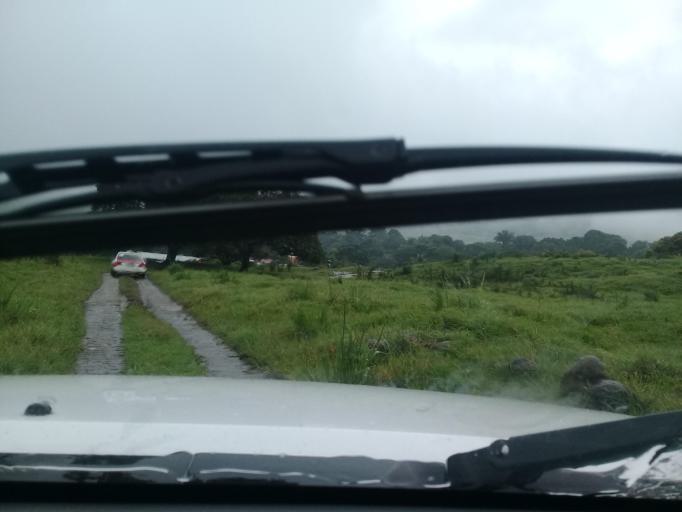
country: MX
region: Veracruz
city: Santiago Tuxtla
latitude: 18.4582
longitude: -95.3262
